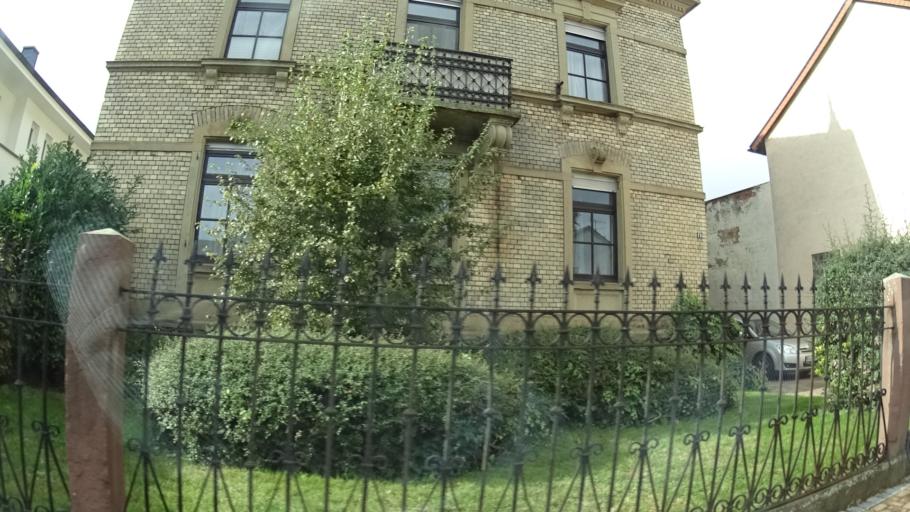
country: DE
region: Baden-Wuerttemberg
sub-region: Karlsruhe Region
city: Ostringen
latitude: 49.2193
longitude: 8.7086
